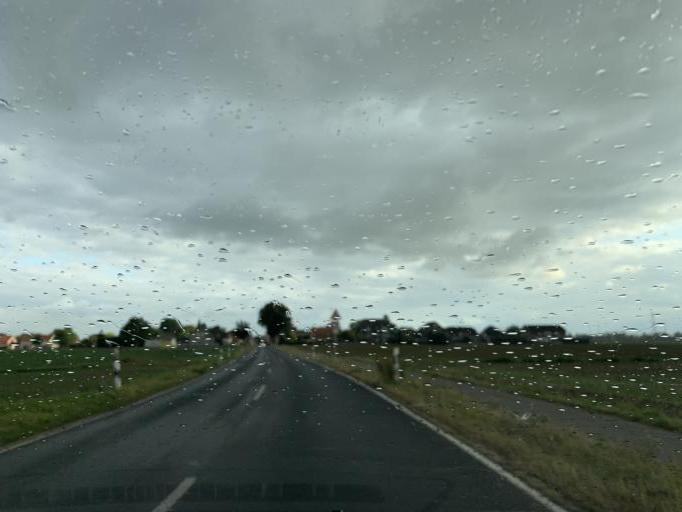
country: DE
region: North Rhine-Westphalia
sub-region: Regierungsbezirk Koln
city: Linnich
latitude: 50.9689
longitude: 6.2720
